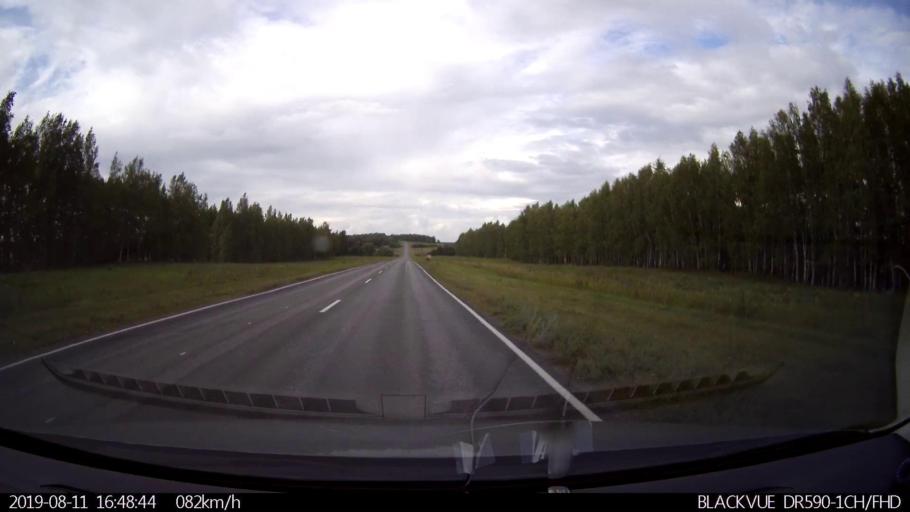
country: RU
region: Ulyanovsk
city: Mayna
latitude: 54.2123
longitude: 47.6933
